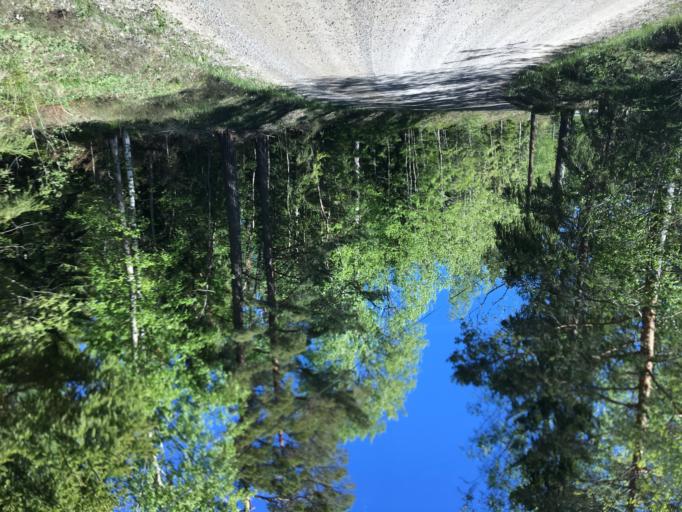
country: SE
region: Soedermanland
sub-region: Eskilstuna Kommun
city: Kvicksund
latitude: 59.3580
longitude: 16.2621
